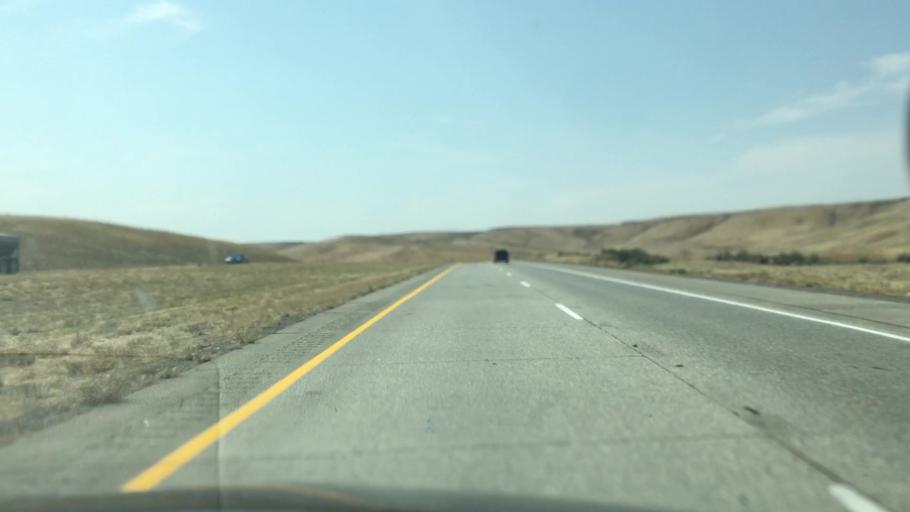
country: US
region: Idaho
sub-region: Elmore County
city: Glenns Ferry
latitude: 42.9642
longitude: -115.3258
